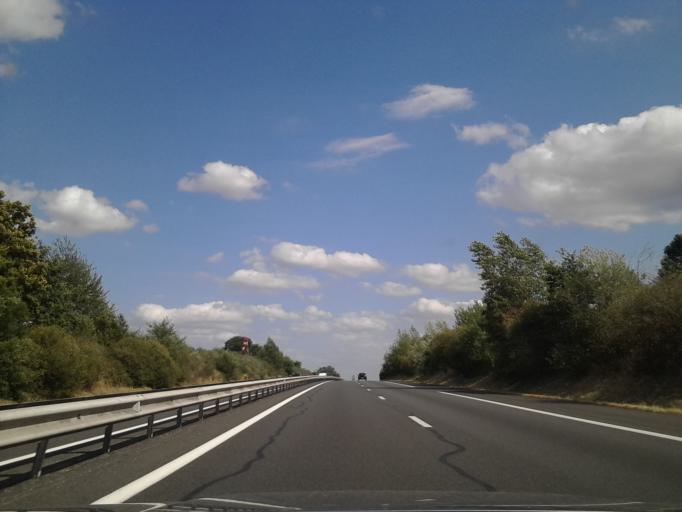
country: FR
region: Auvergne
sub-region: Departement de l'Allier
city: Doyet
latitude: 46.3419
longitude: 2.8781
